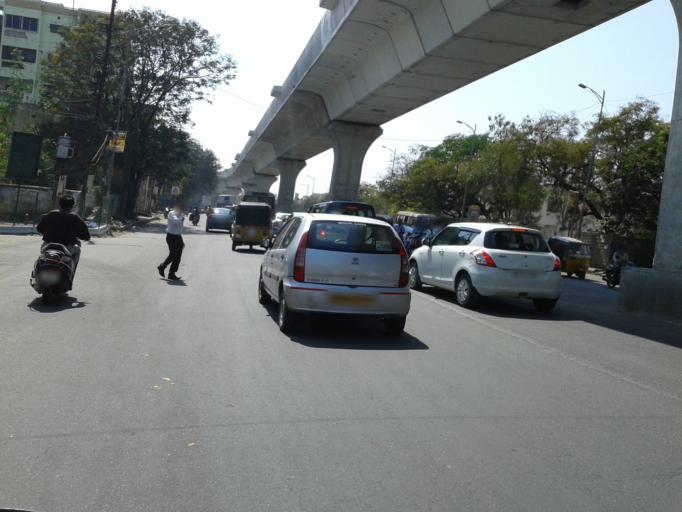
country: IN
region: Telangana
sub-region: Hyderabad
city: Malkajgiri
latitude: 17.4395
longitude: 78.5052
